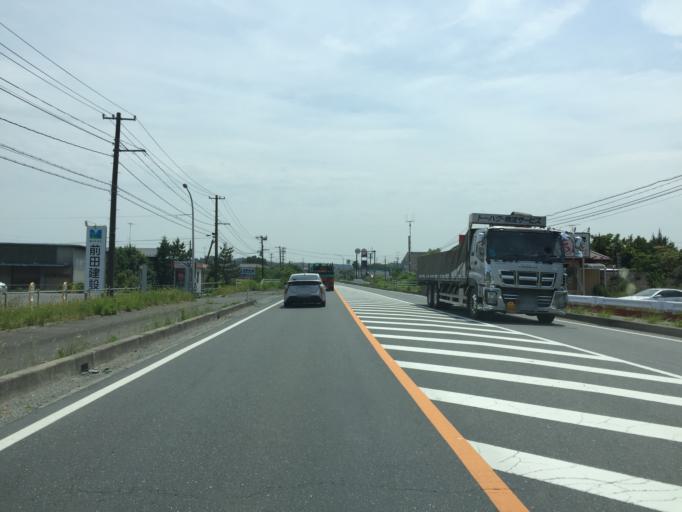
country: JP
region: Fukushima
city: Namie
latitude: 37.4572
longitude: 141.0104
